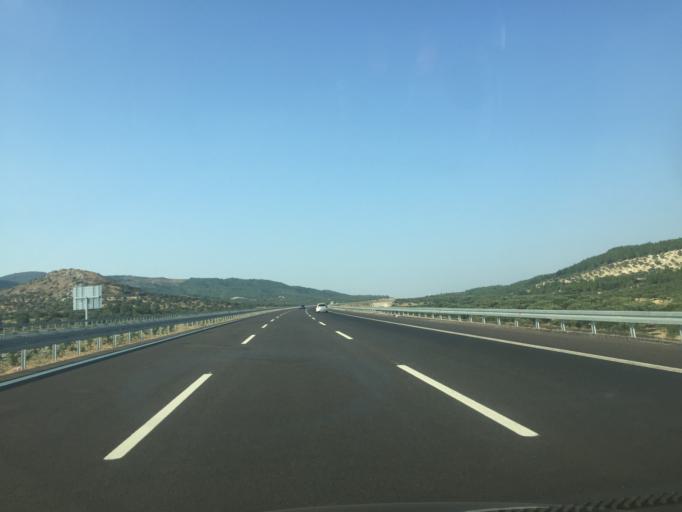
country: TR
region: Manisa
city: Zeytinliova
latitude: 38.9861
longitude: 27.7321
